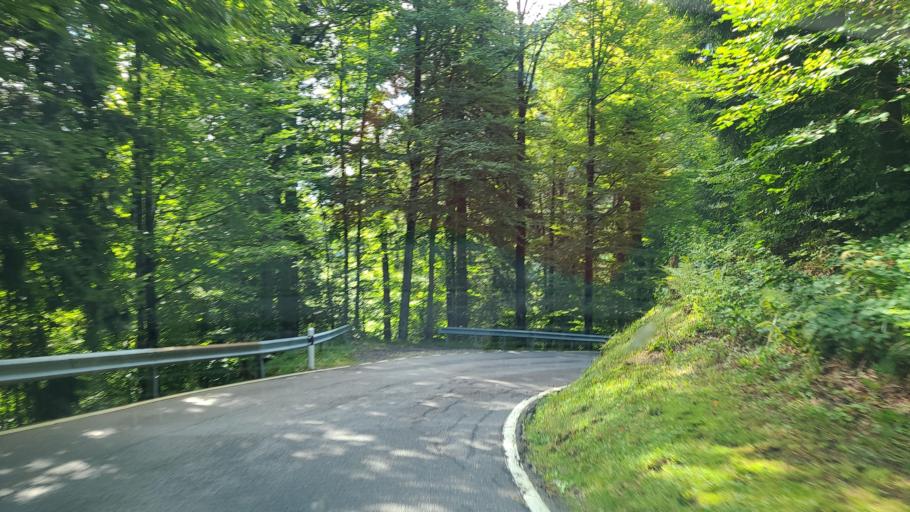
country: CH
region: Schwyz
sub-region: Bezirk March
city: Vorderthal
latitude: 47.1323
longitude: 8.8828
